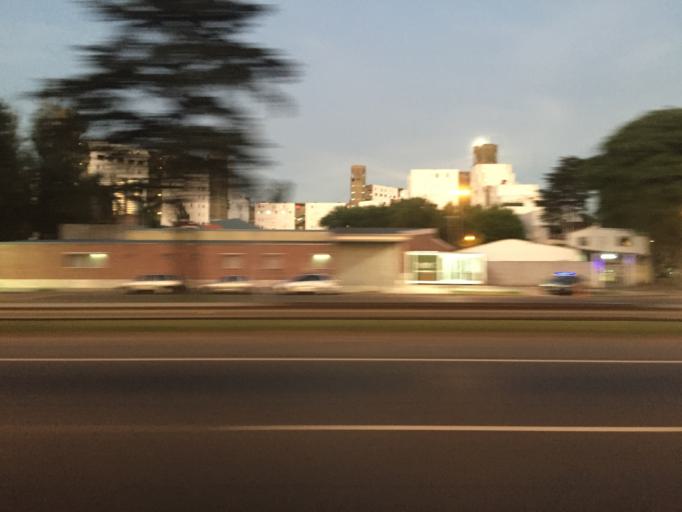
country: AR
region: Buenos Aires F.D.
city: Villa Lugano
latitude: -34.6801
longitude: -58.4943
